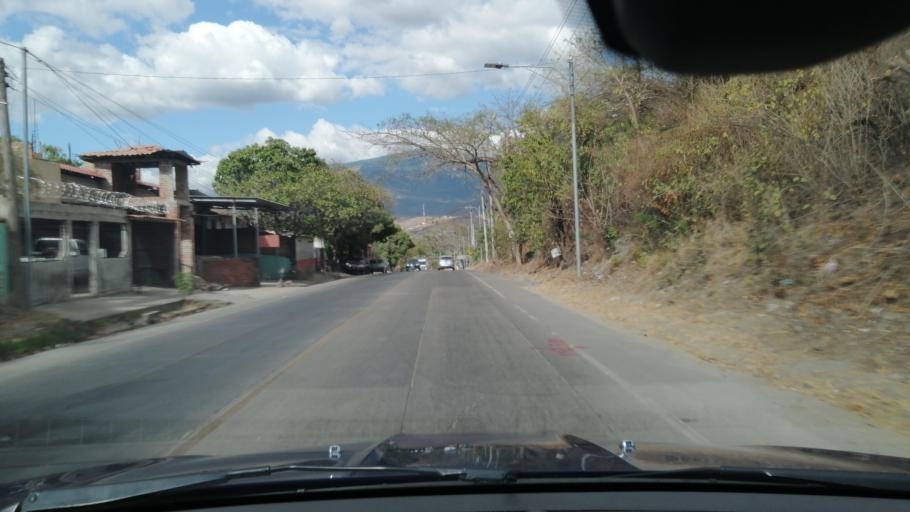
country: SV
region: Santa Ana
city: Metapan
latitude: 14.3171
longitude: -89.4465
